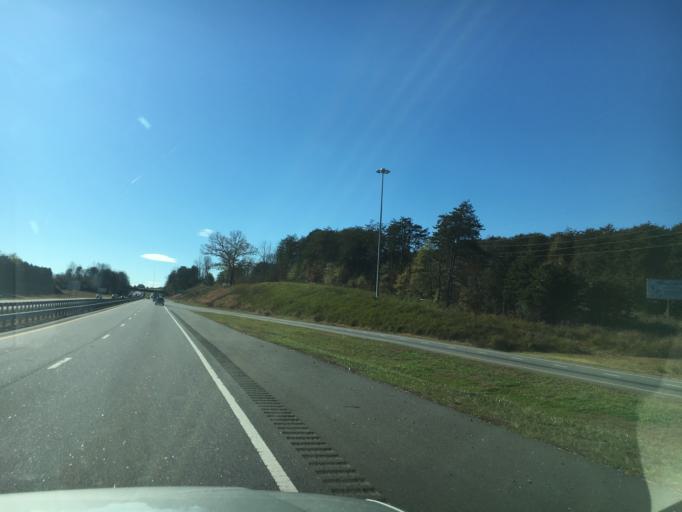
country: US
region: North Carolina
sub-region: Burke County
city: Morganton
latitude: 35.7220
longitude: -81.6581
